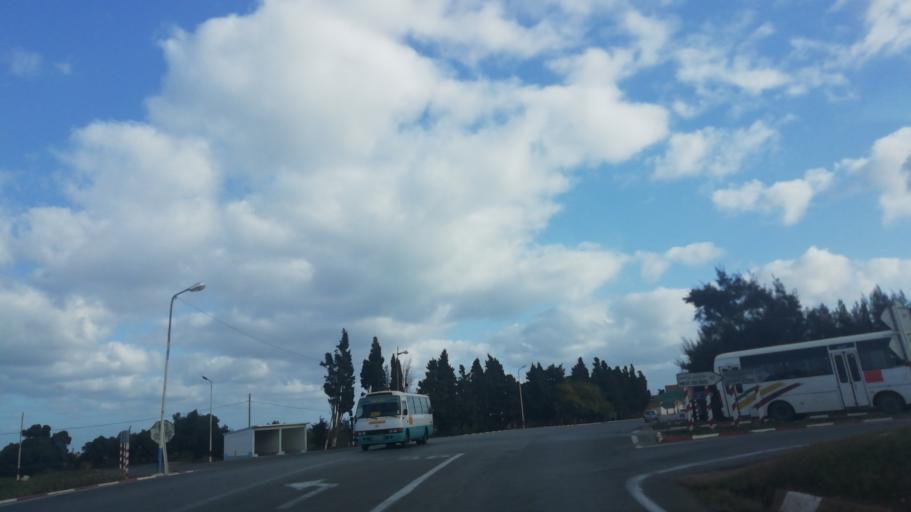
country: DZ
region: Relizane
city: Mazouna
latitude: 36.2449
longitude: 0.5370
